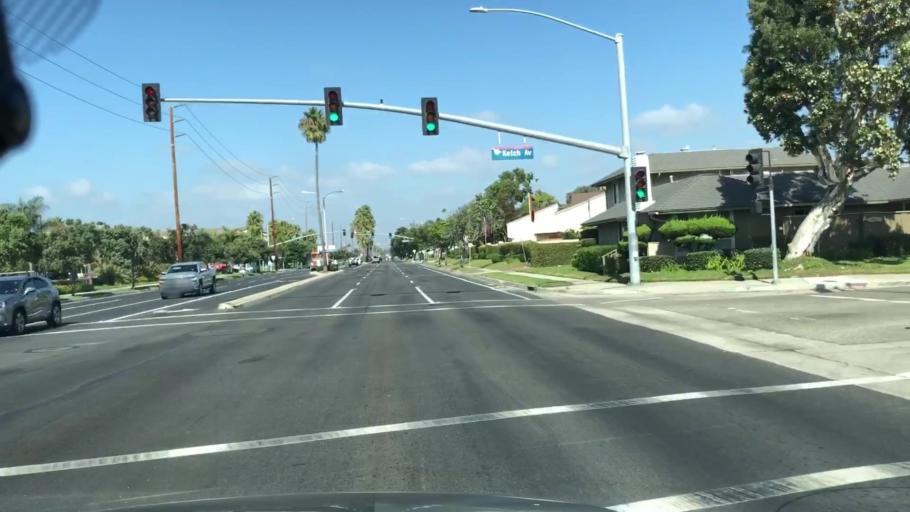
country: US
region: California
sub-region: Ventura County
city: Oxnard Shores
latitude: 34.1839
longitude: -119.2213
